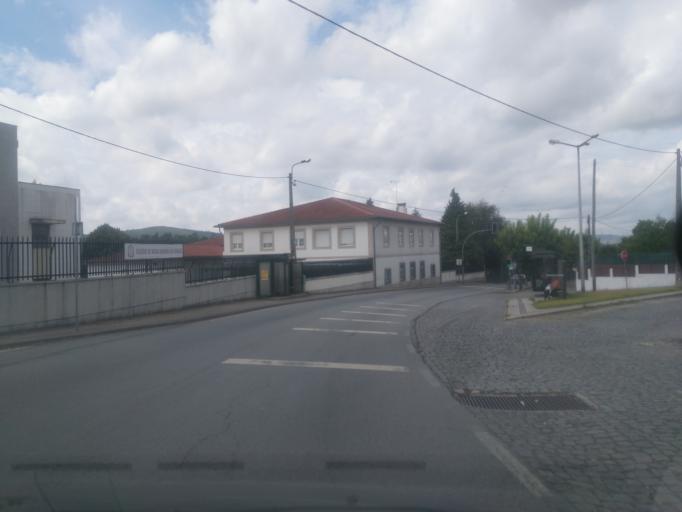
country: PT
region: Braga
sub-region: Braga
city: Braga
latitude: 41.5538
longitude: -8.4400
